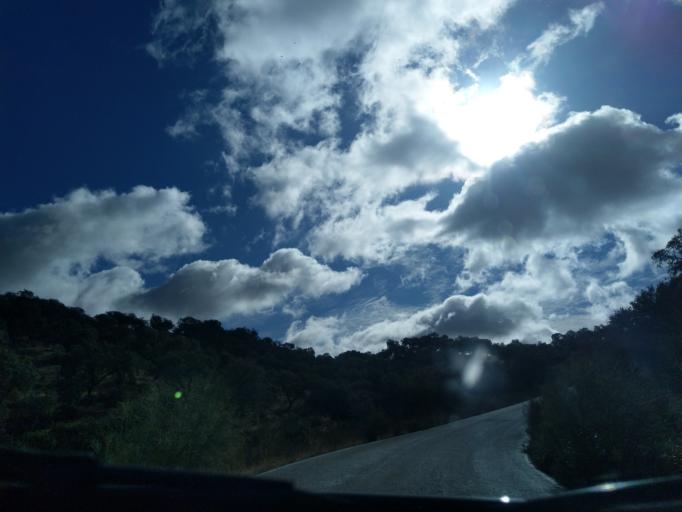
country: ES
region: Extremadura
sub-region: Provincia de Badajoz
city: Reina
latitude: 38.1316
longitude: -5.9161
